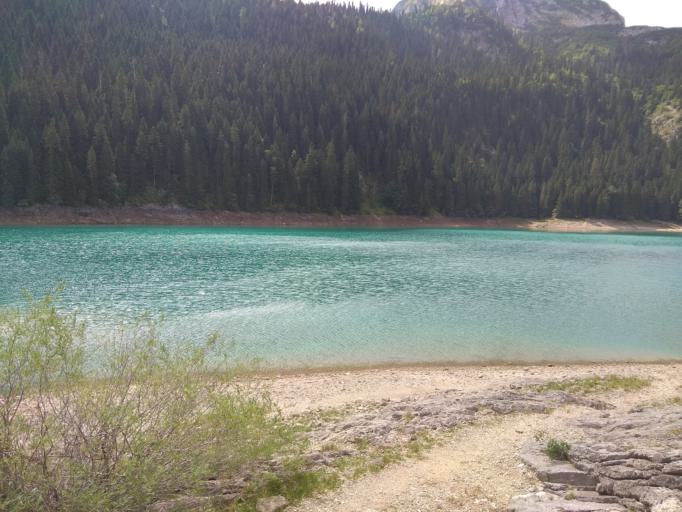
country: ME
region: Opstina Zabljak
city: Zabljak
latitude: 43.1447
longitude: 19.0900
